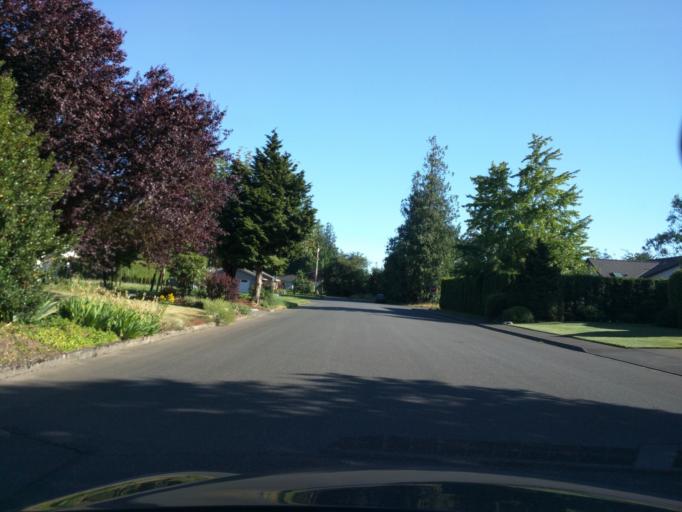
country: US
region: Washington
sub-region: Whatcom County
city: Lynden
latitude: 48.9536
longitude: -122.4577
